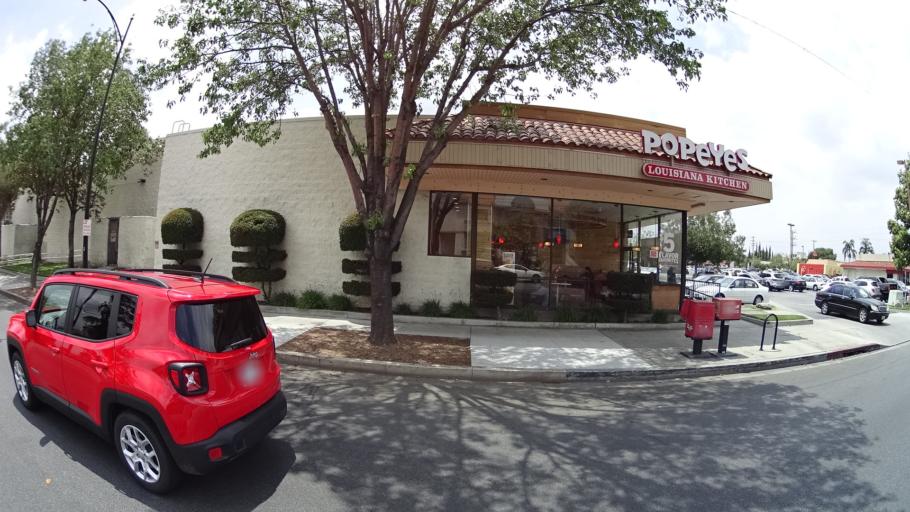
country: US
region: California
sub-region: Los Angeles County
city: Universal City
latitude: 34.1601
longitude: -118.3433
